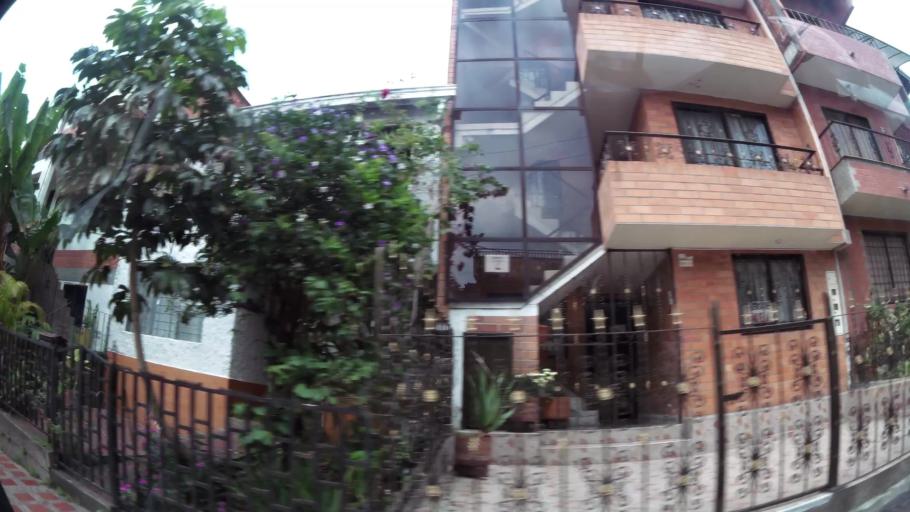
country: CO
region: Antioquia
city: Envigado
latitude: 6.1588
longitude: -75.5921
